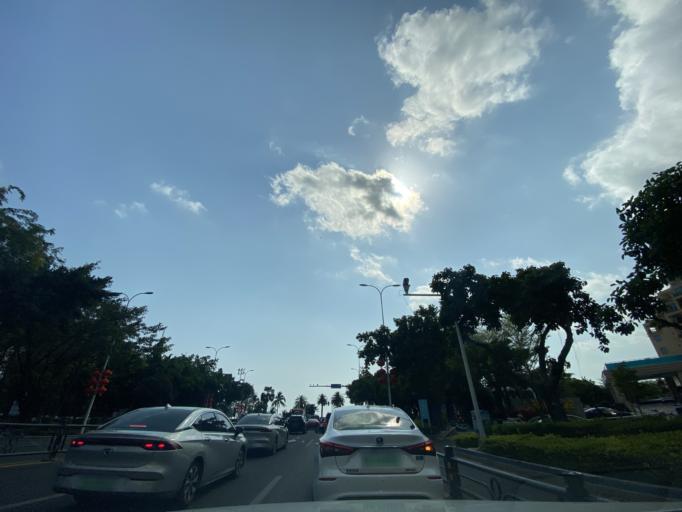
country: CN
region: Hainan
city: Sanya
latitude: 18.2620
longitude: 109.4911
